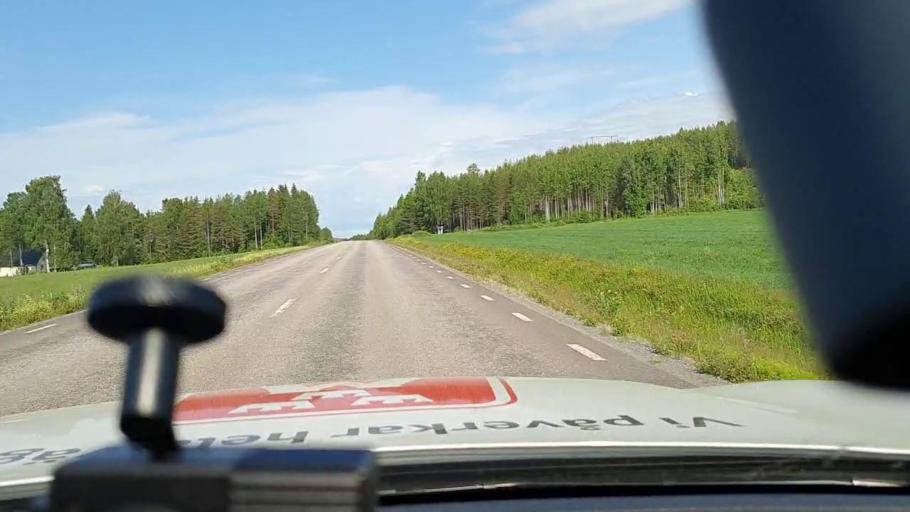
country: SE
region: Norrbotten
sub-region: Bodens Kommun
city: Boden
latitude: 65.9142
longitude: 21.3405
